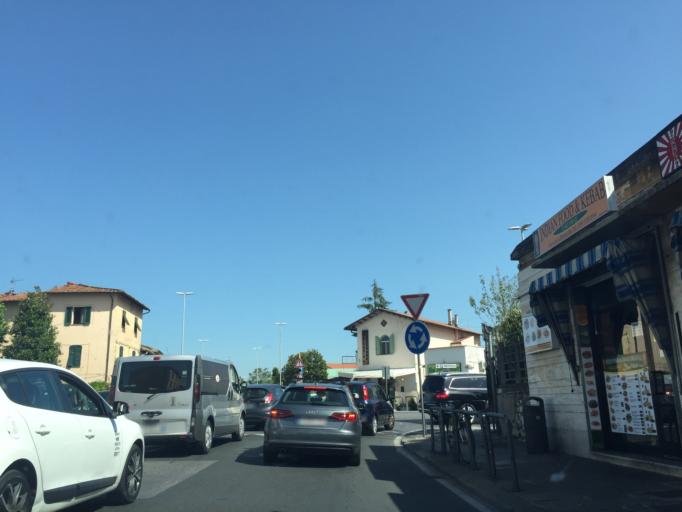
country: IT
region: Tuscany
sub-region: Province of Pisa
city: Pisa
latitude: 43.7247
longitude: 10.3914
